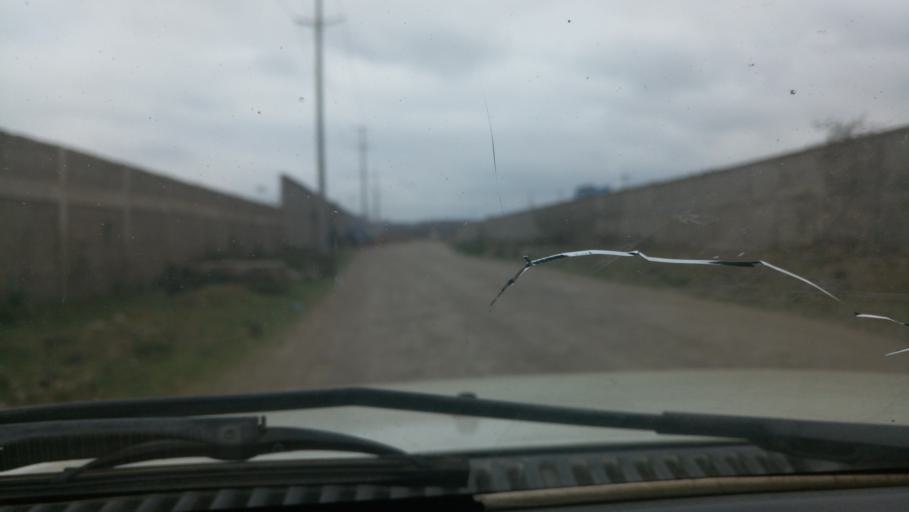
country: KE
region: Nairobi Area
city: Pumwani
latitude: -1.3378
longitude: 36.8862
